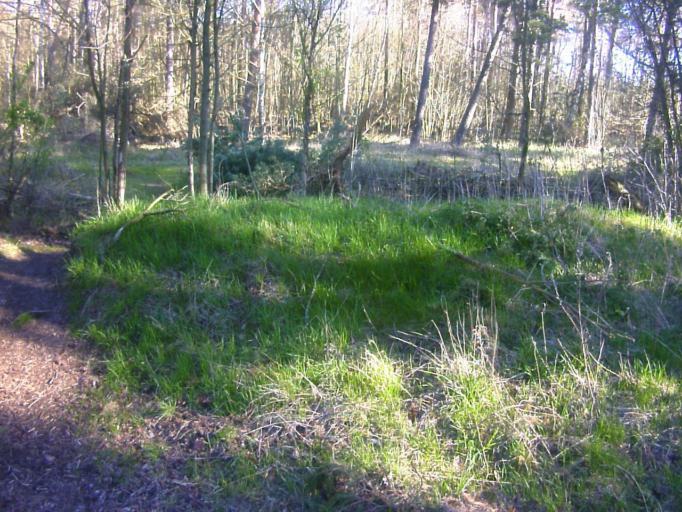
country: SE
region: Skane
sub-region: Kavlinge Kommun
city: Hofterup
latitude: 55.8192
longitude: 12.9667
